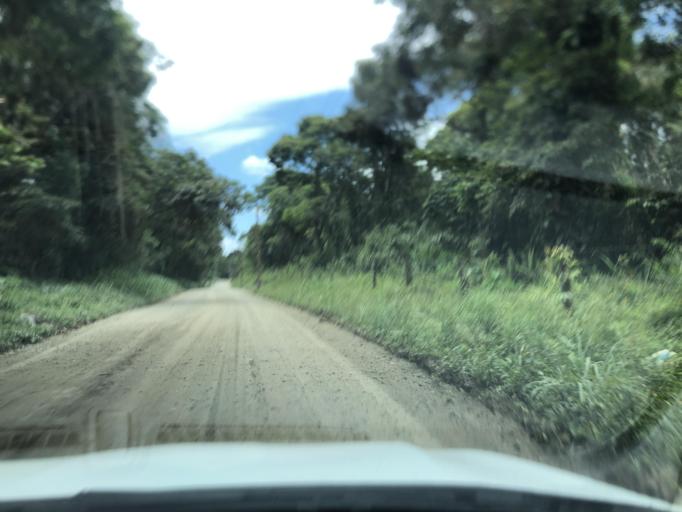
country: BR
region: Santa Catarina
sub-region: Sao Francisco Do Sul
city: Sao Francisco do Sul
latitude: -26.2265
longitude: -48.5989
